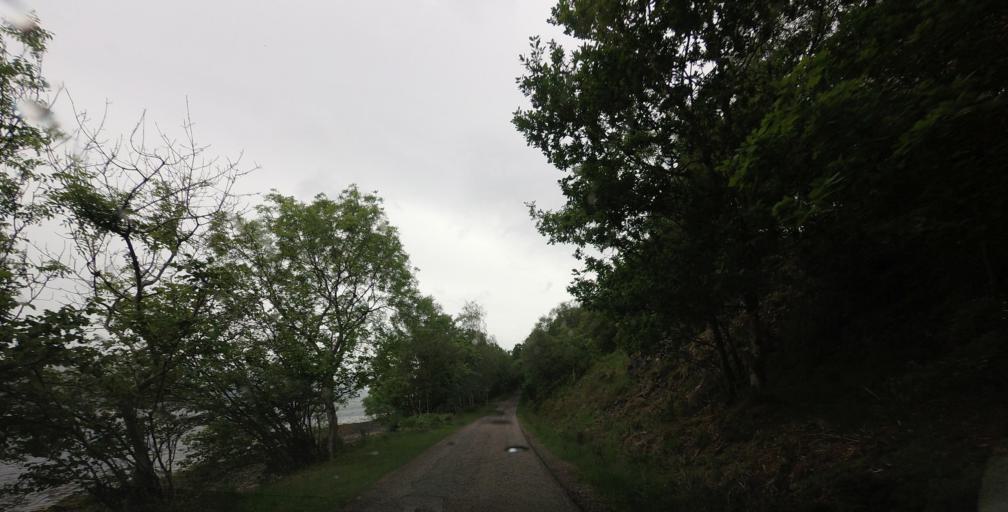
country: GB
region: Scotland
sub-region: Highland
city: Fort William
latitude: 56.8112
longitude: -5.1445
